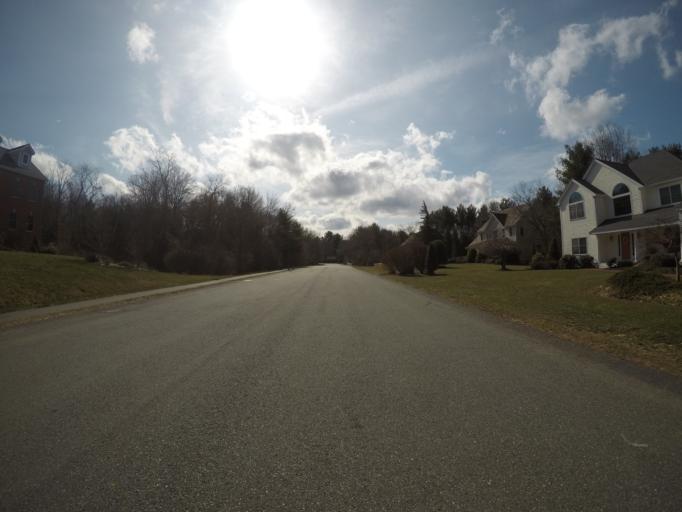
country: US
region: Massachusetts
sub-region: Bristol County
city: Easton
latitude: 42.0130
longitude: -71.1510
